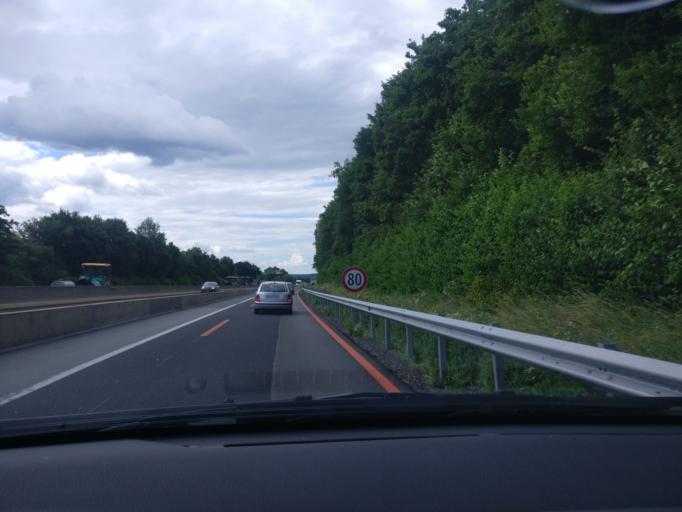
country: AT
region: Styria
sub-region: Politischer Bezirk Hartberg-Fuerstenfeld
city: Sankt Johann in der Haide
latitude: 47.2535
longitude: 16.0014
